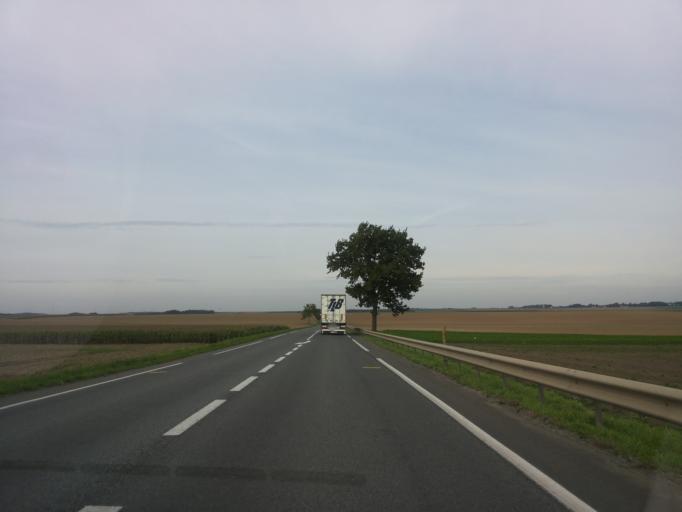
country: FR
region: Nord-Pas-de-Calais
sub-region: Departement du Pas-de-Calais
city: Marquion
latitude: 50.2207
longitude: 3.0482
